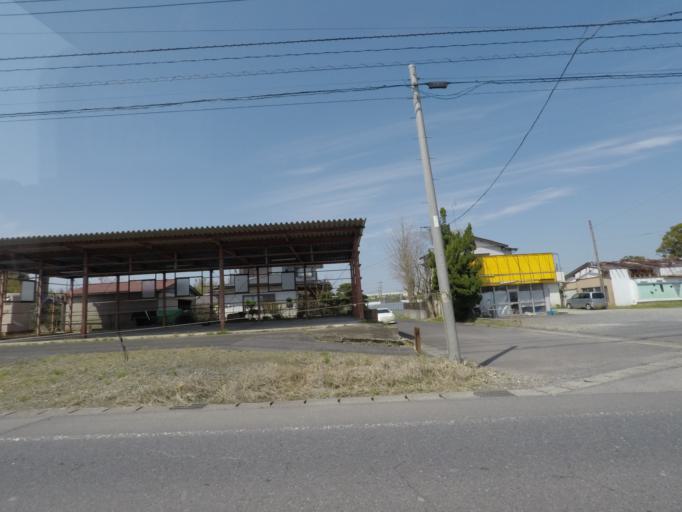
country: JP
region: Chiba
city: Narita
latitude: 35.8269
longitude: 140.3013
